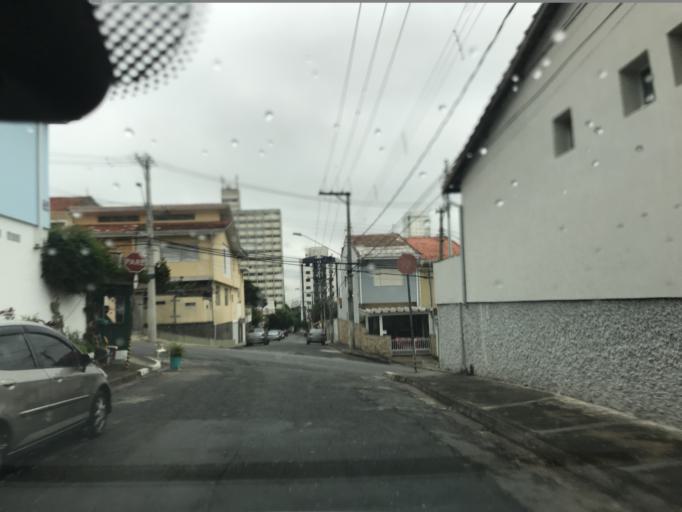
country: BR
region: Sao Paulo
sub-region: Sao Paulo
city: Sao Paulo
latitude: -23.5394
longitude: -46.6768
